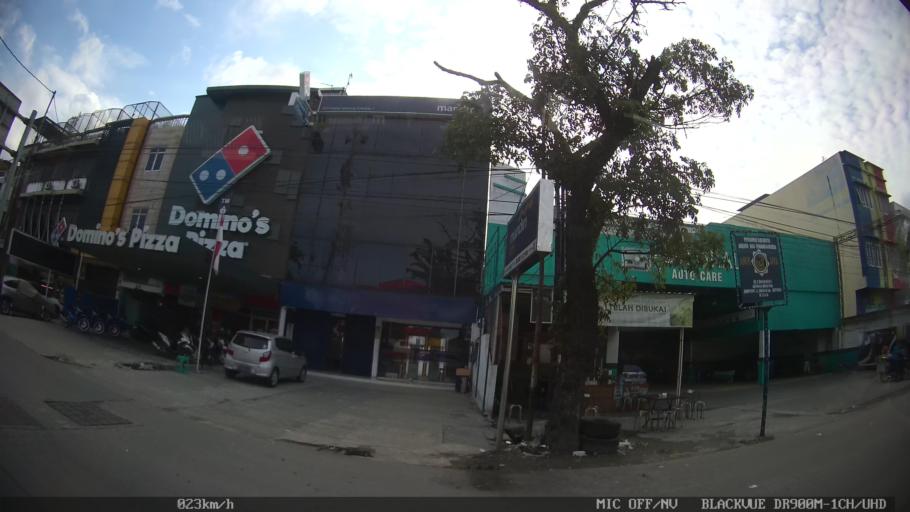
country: ID
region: North Sumatra
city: Medan
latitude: 3.6270
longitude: 98.6809
